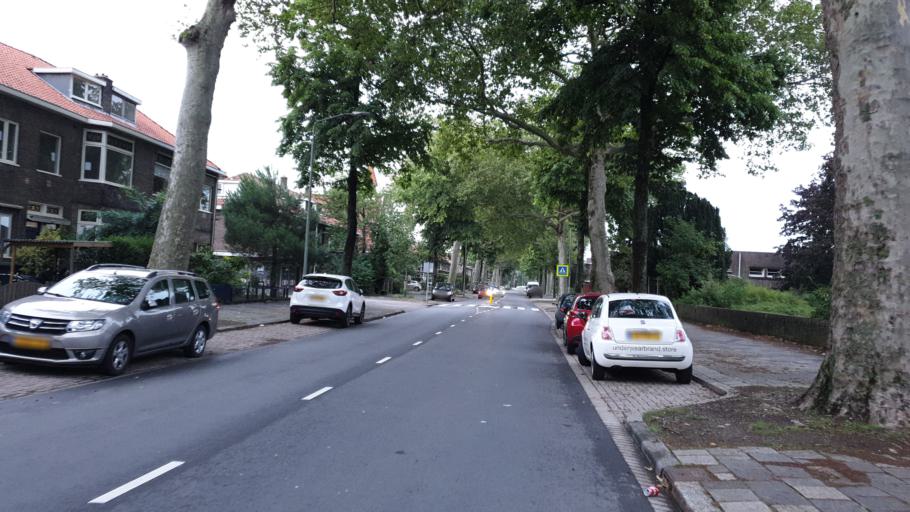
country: NL
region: South Holland
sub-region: Gemeente Dordrecht
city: Dordrecht
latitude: 51.8026
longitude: 4.6596
